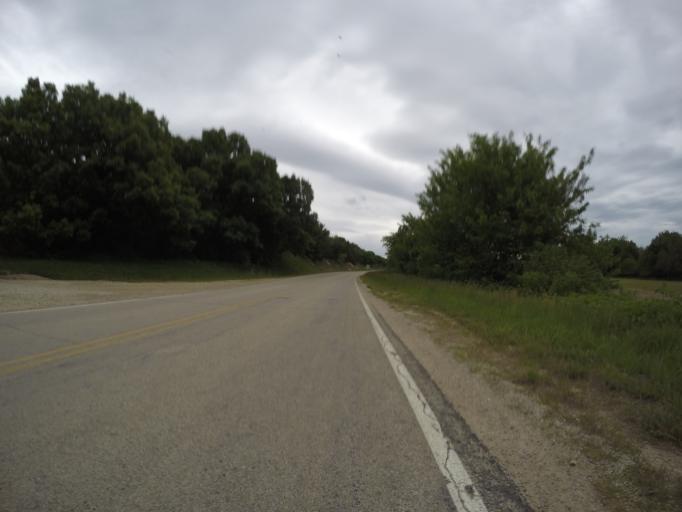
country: US
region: Kansas
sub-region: Pottawatomie County
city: Wamego
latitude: 39.1843
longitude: -96.3453
